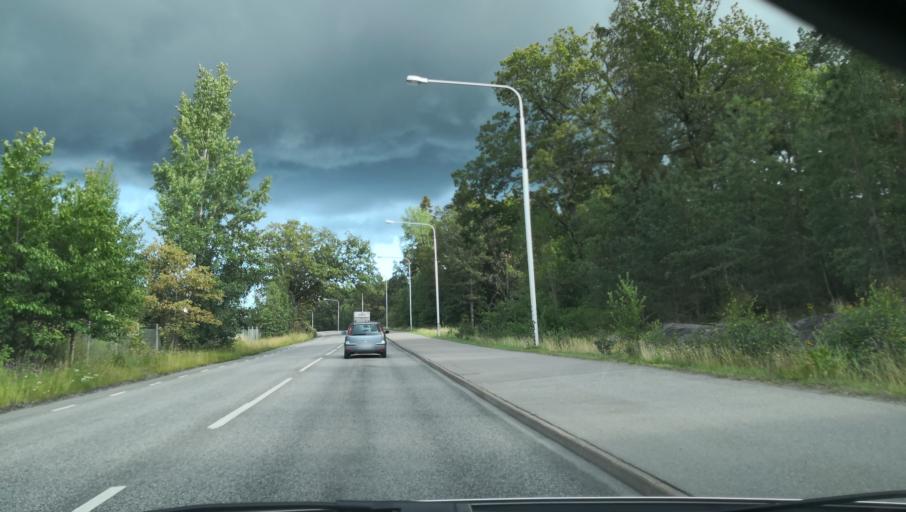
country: SE
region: Stockholm
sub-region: Stockholms Kommun
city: Arsta
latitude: 59.2463
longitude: 18.0674
